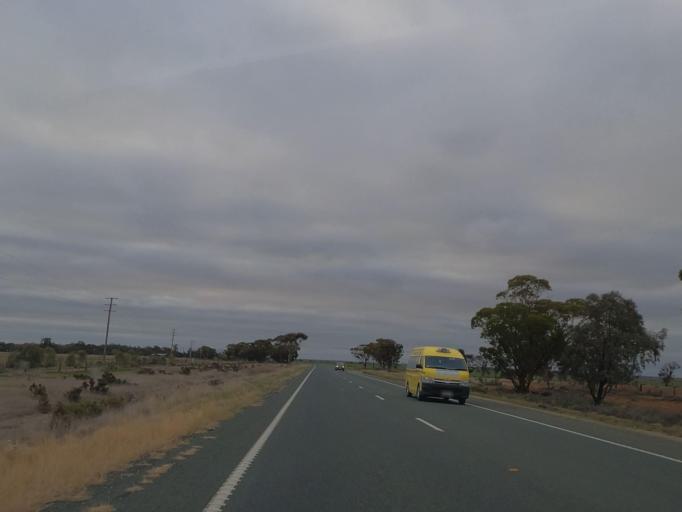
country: AU
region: Victoria
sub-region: Swan Hill
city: Swan Hill
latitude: -35.5655
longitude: 143.7838
